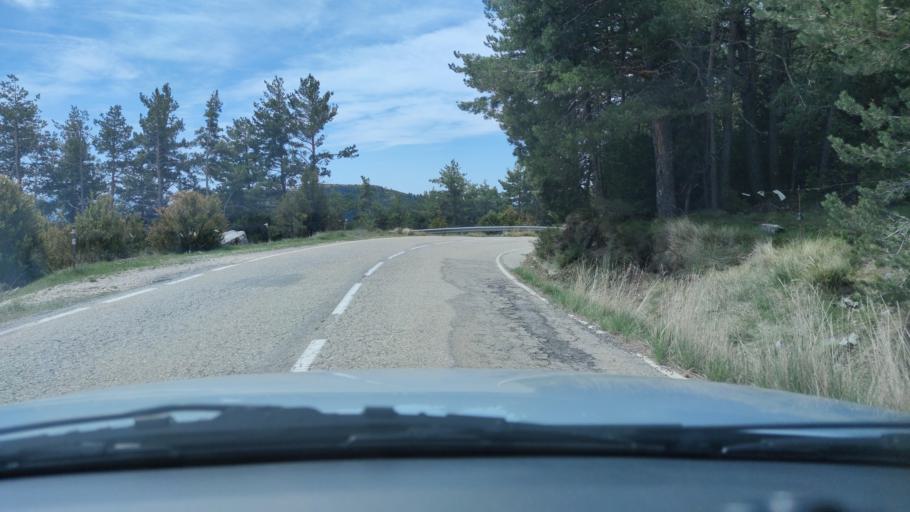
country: ES
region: Catalonia
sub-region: Provincia de Lleida
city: Olius
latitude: 42.1472
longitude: 1.5552
